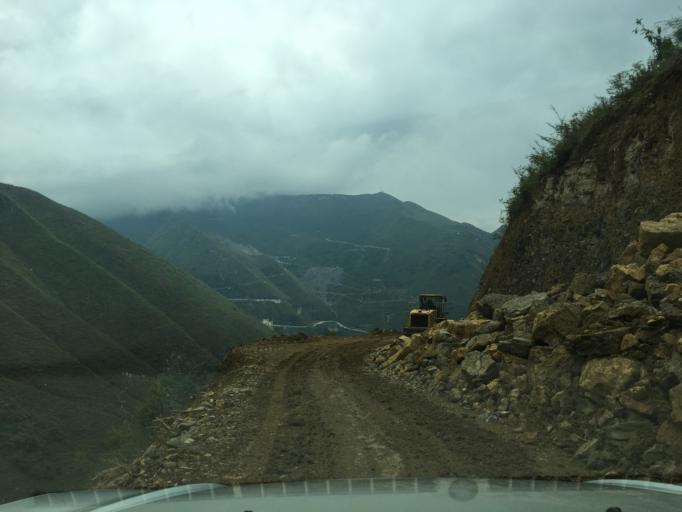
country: CN
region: Guizhou Sheng
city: Liupanshui
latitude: 25.9637
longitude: 105.2367
